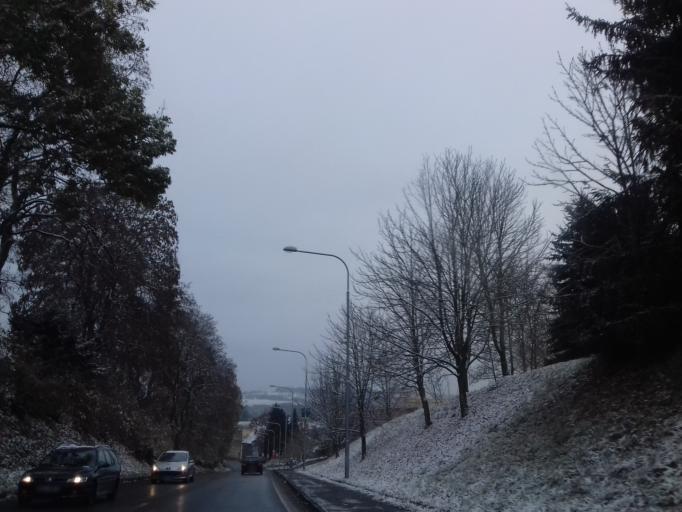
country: CZ
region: Plzensky
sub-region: Okres Domazlice
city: Domazlice
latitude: 49.4454
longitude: 12.9319
